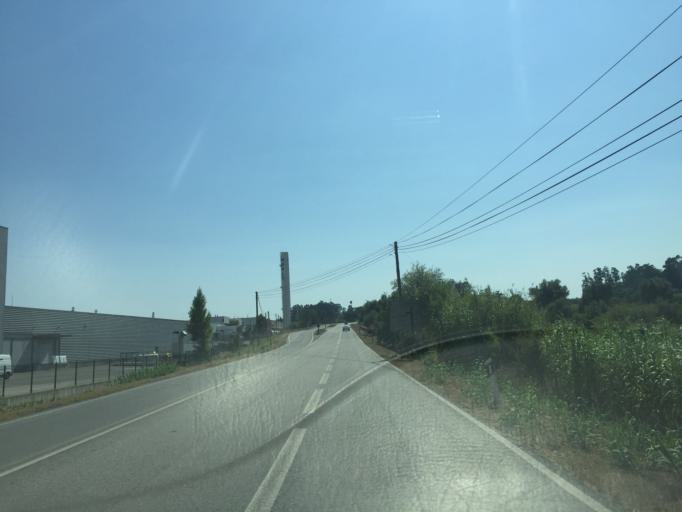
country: PT
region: Aveiro
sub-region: Mealhada
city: Mealhada
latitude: 40.3690
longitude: -8.4890
